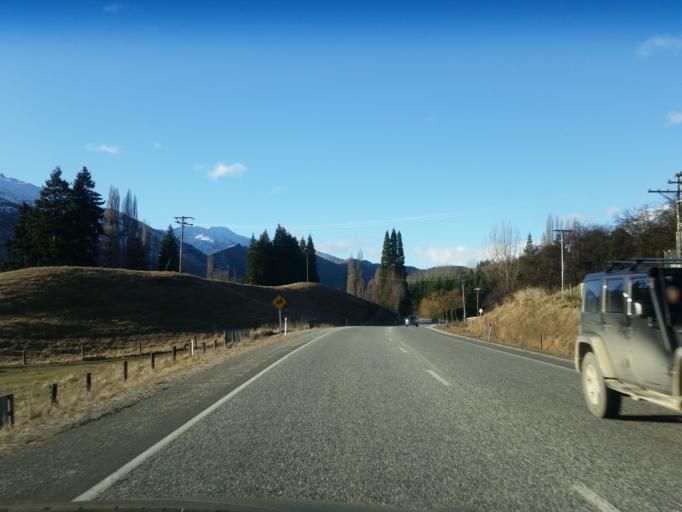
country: NZ
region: Otago
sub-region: Queenstown-Lakes District
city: Queenstown
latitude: -44.9618
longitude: 168.7208
